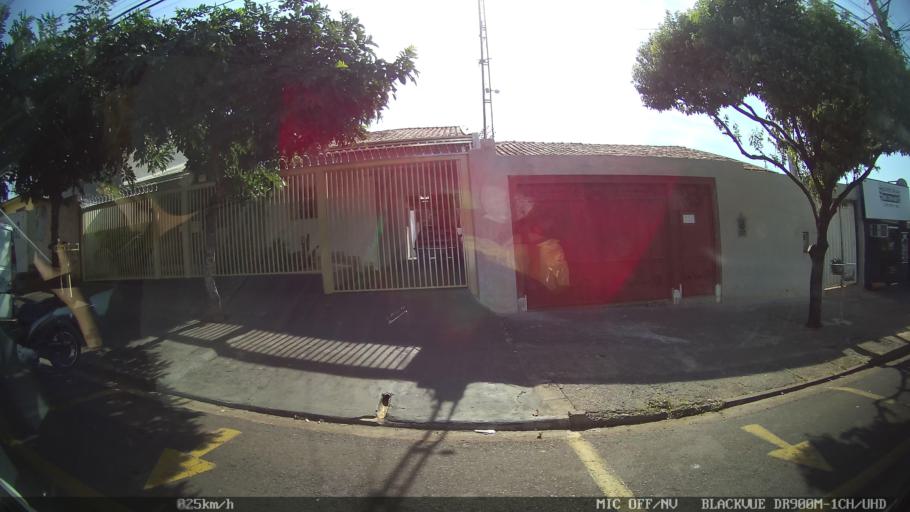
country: BR
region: Sao Paulo
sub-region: Sao Jose Do Rio Preto
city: Sao Jose do Rio Preto
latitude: -20.7932
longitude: -49.4066
